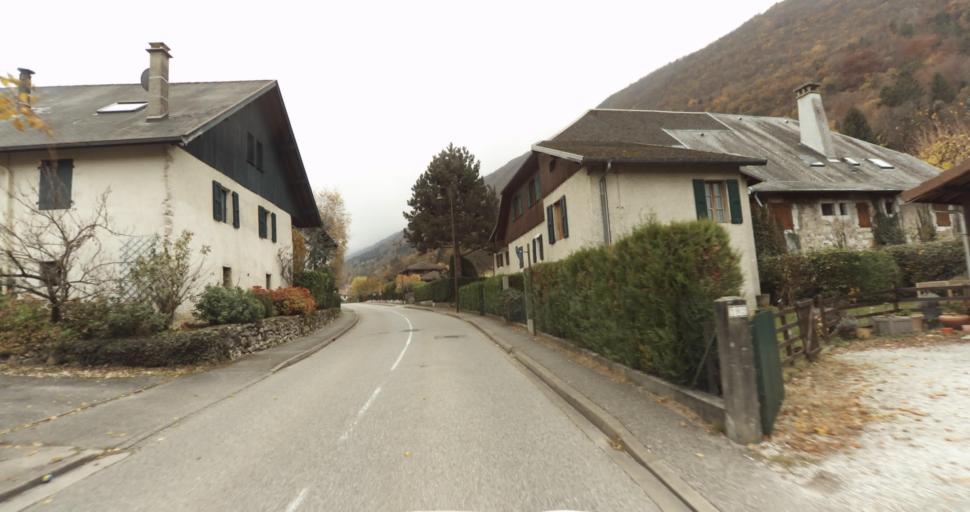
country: FR
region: Rhone-Alpes
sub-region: Departement de la Haute-Savoie
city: Sevrier
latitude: 45.8607
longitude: 6.1387
